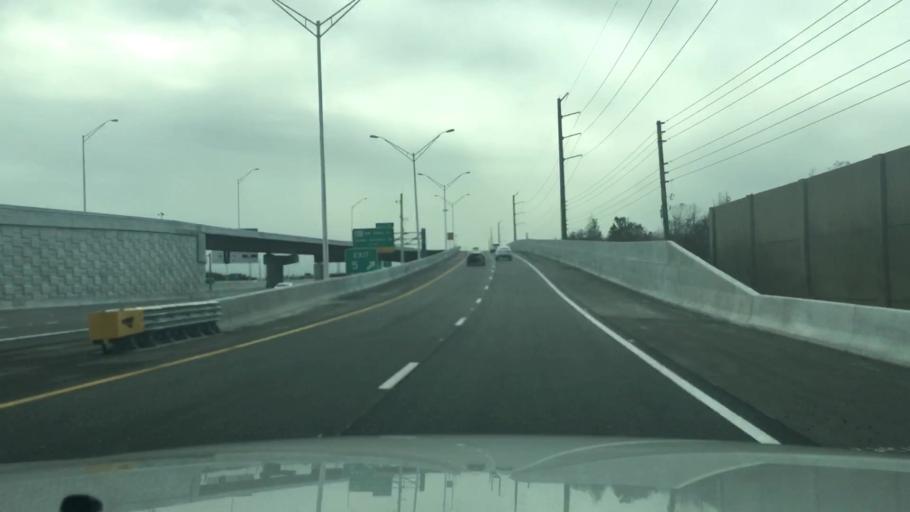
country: US
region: Florida
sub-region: Miami-Dade County
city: Palm Springs North
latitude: 25.9621
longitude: -80.3526
